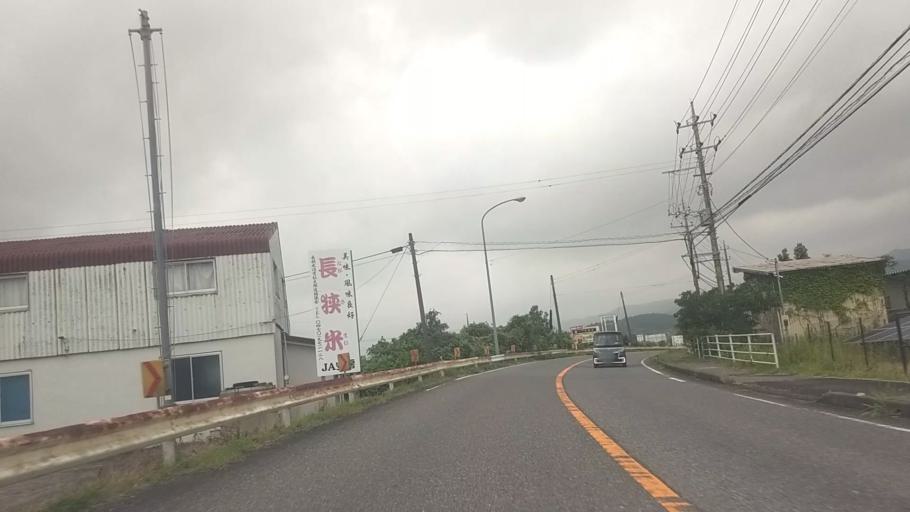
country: JP
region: Chiba
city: Kawaguchi
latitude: 35.1274
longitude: 140.0464
